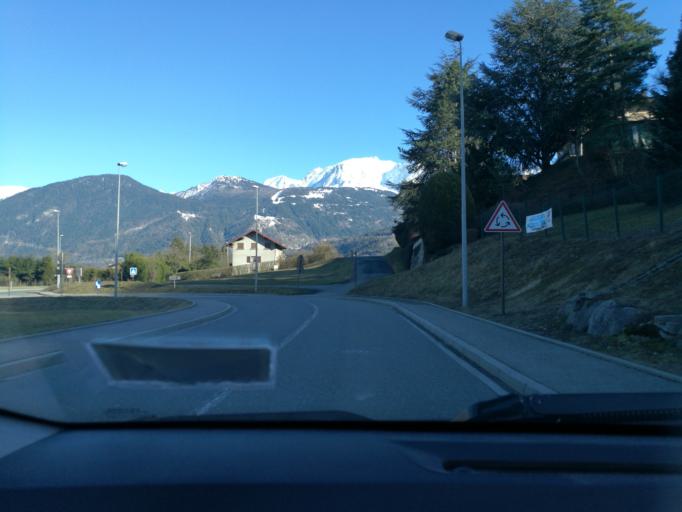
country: FR
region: Rhone-Alpes
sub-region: Departement de la Haute-Savoie
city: Domancy
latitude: 45.9099
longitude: 6.6570
